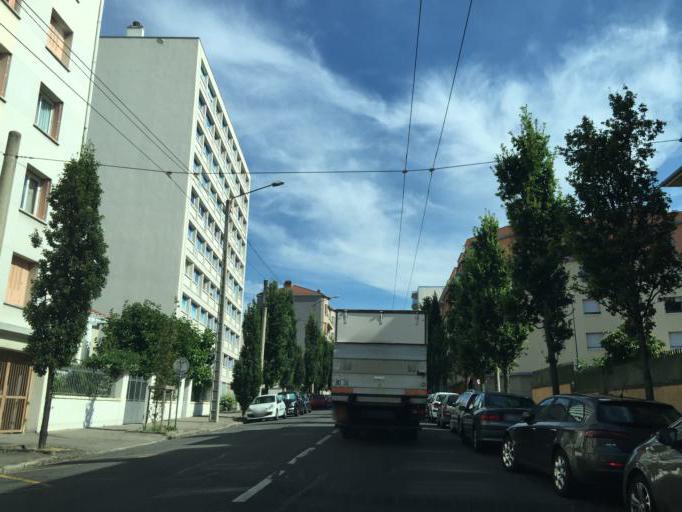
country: FR
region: Rhone-Alpes
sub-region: Departement de la Loire
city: Saint-Etienne
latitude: 45.4188
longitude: 4.3997
